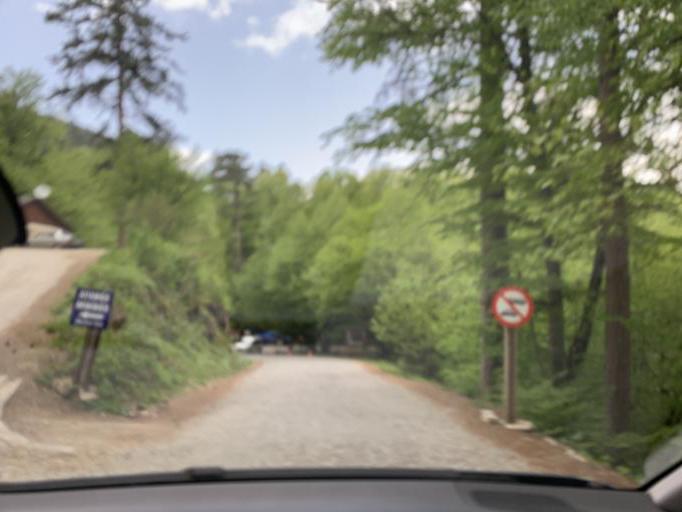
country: TR
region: Zonguldak
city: Egerci
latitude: 40.9380
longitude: 31.7409
